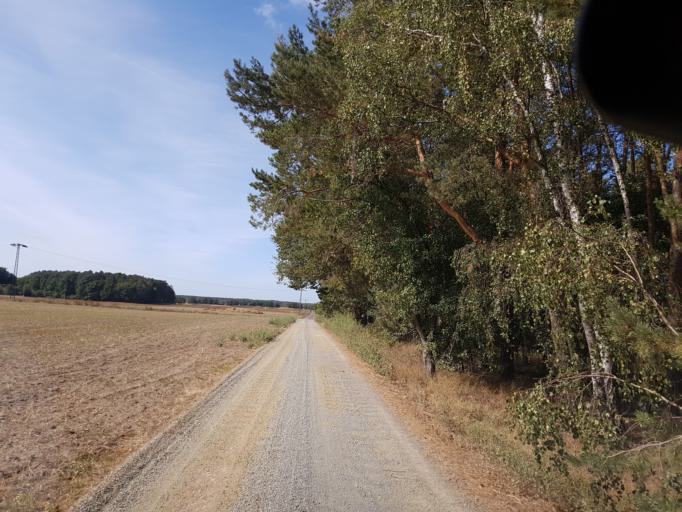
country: DE
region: Brandenburg
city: Sonnewalde
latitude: 51.7567
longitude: 13.6341
